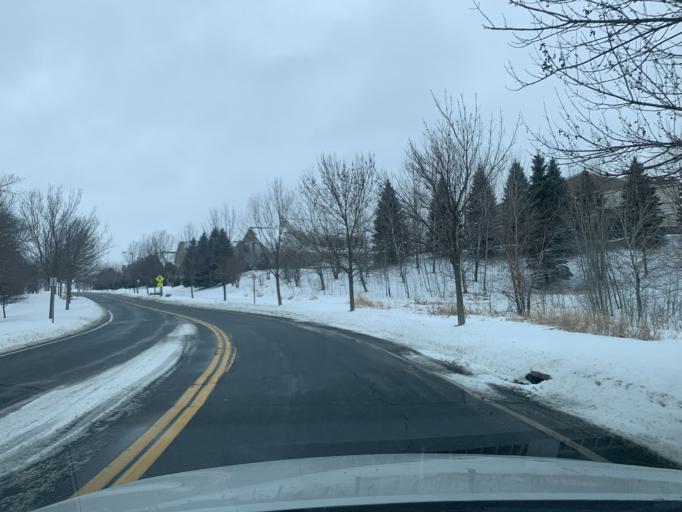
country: US
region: Minnesota
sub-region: Carver County
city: Victoria
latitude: 44.8381
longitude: -93.6531
